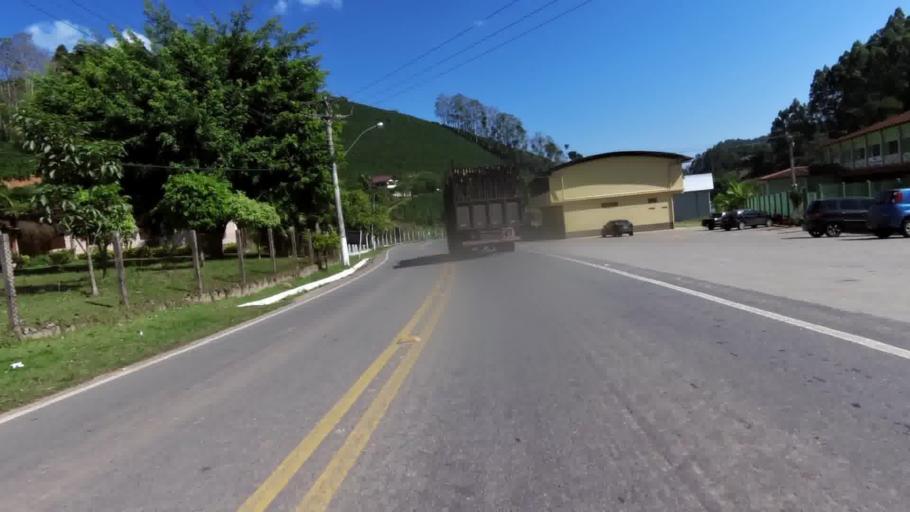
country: BR
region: Espirito Santo
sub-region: Marechal Floriano
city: Marechal Floriano
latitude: -20.4421
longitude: -40.7805
